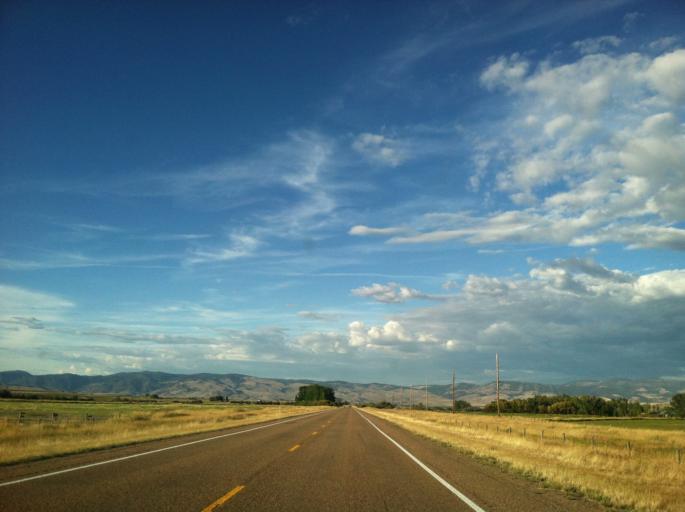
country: US
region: Montana
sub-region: Granite County
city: Philipsburg
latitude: 46.5580
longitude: -113.2151
